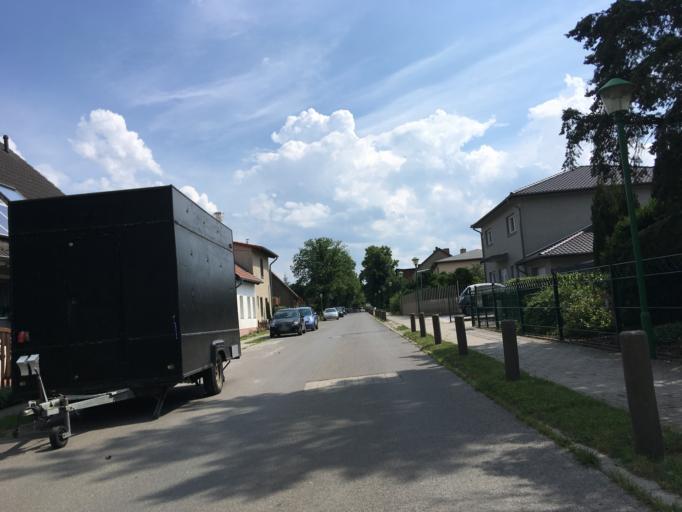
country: DE
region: Brandenburg
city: Glienicke
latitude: 52.6603
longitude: 13.3361
